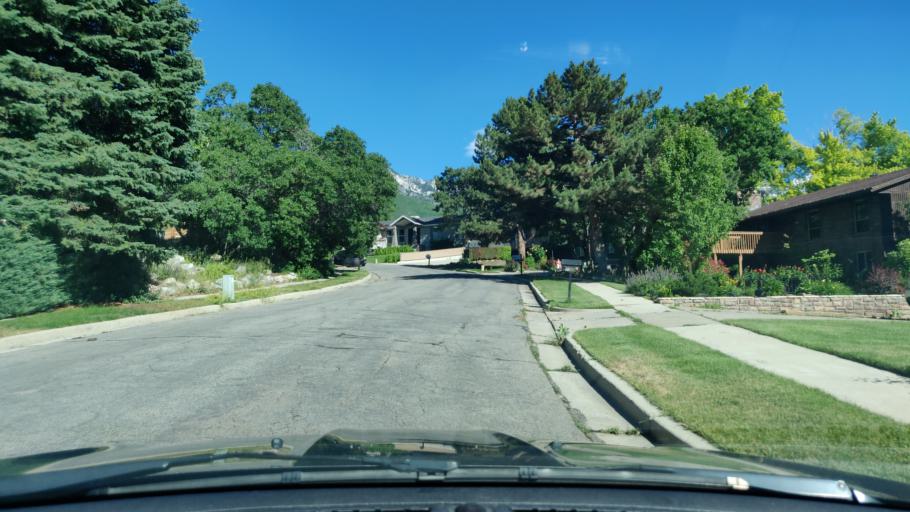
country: US
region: Utah
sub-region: Salt Lake County
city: Cottonwood Heights
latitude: 40.6135
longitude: -111.8097
